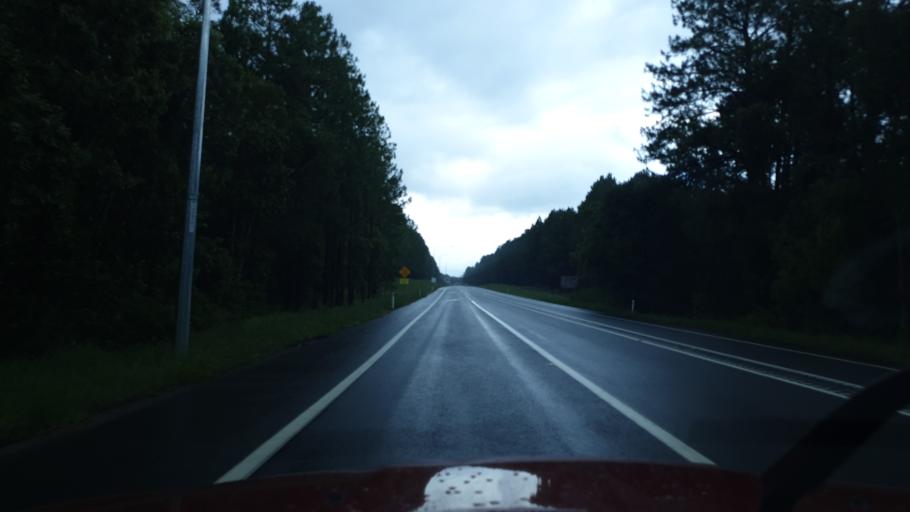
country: AU
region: Queensland
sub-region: Moreton Bay
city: Caboolture
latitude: -26.9842
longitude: 152.9723
